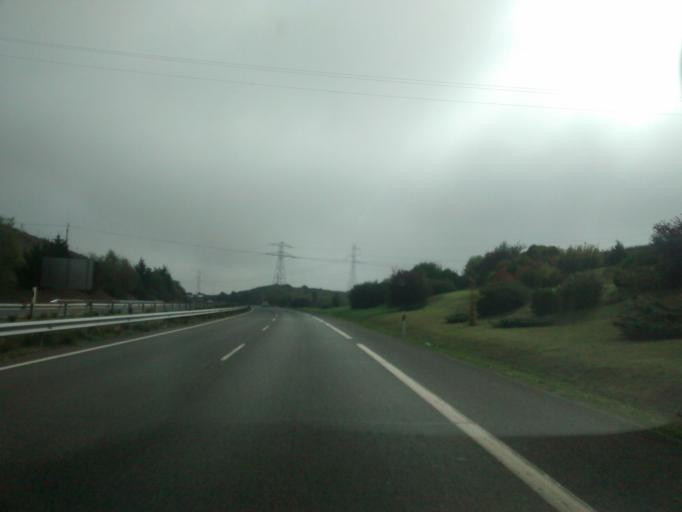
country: ES
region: Basque Country
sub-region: Provincia de Alava
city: Gasteiz / Vitoria
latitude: 42.8801
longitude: -2.6840
